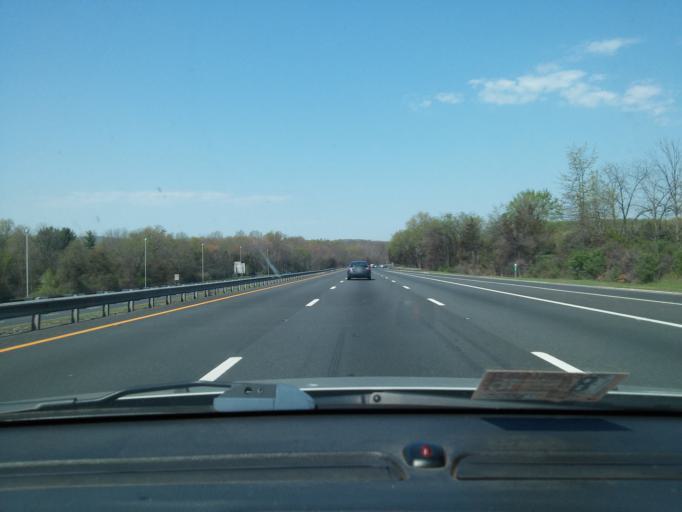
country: US
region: New Jersey
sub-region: Hunterdon County
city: Whitehouse Station
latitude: 40.6509
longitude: -74.7568
